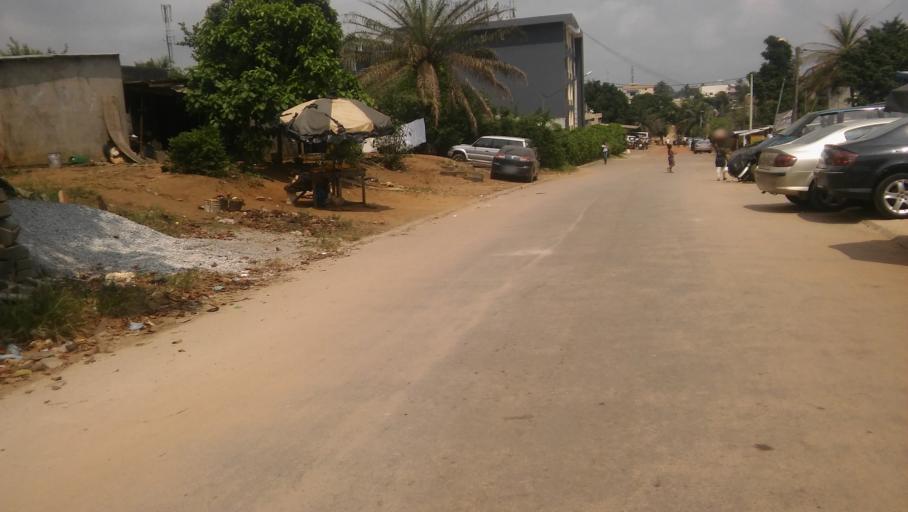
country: CI
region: Lagunes
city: Abidjan
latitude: 5.3576
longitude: -3.9772
